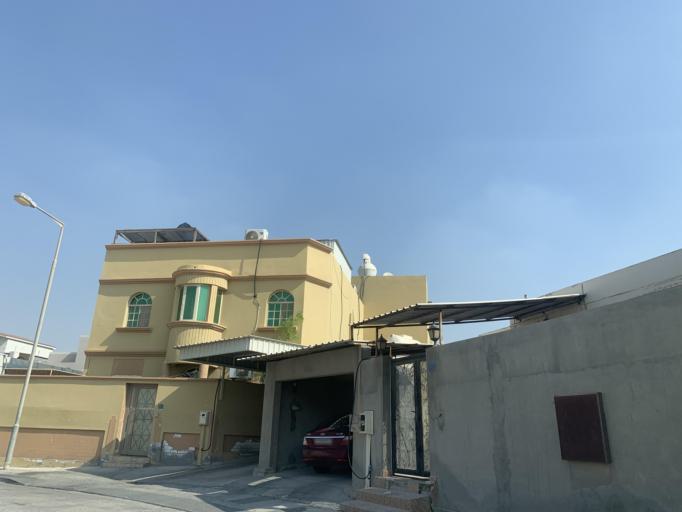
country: BH
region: Central Governorate
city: Madinat Hamad
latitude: 26.1290
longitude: 50.4965
